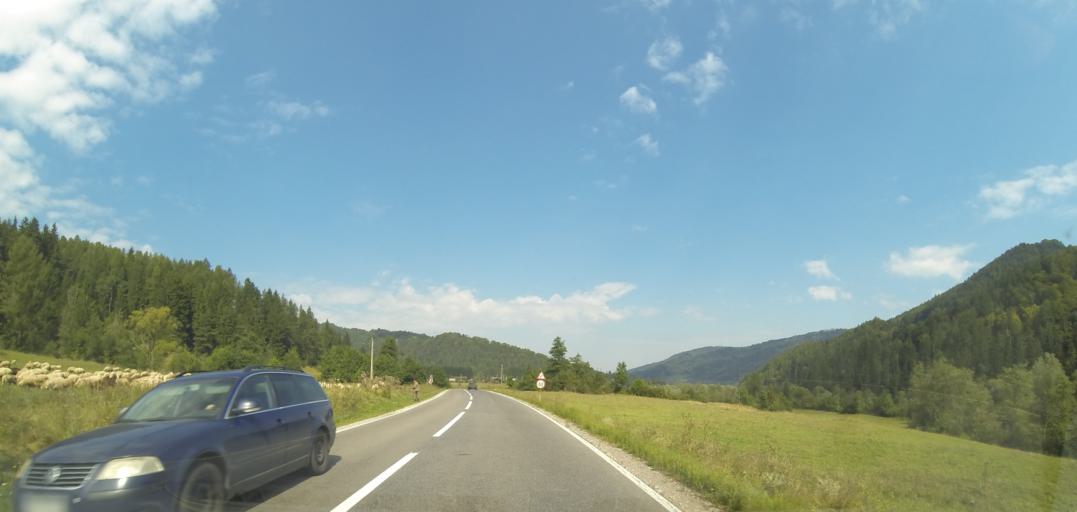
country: RO
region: Brasov
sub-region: Comuna Tarlungeni
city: Zizin
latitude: 45.5553
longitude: 25.7752
